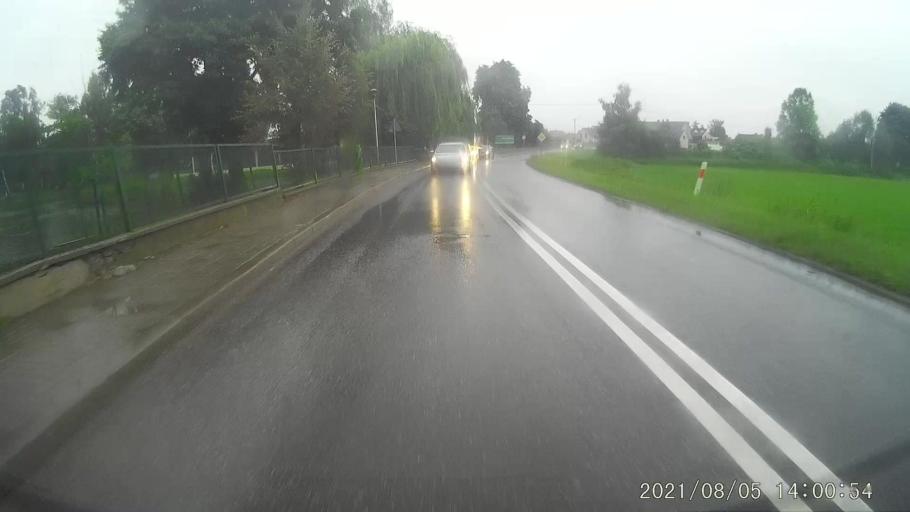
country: PL
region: Opole Voivodeship
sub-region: Powiat krapkowicki
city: Strzeleczki
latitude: 50.4487
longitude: 17.8975
